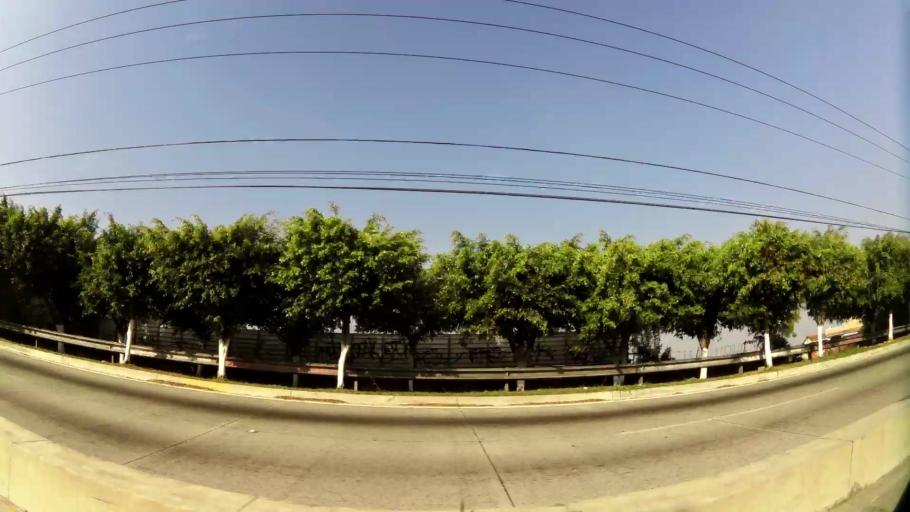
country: SV
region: San Salvador
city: San Salvador
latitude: 13.6762
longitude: -89.2190
